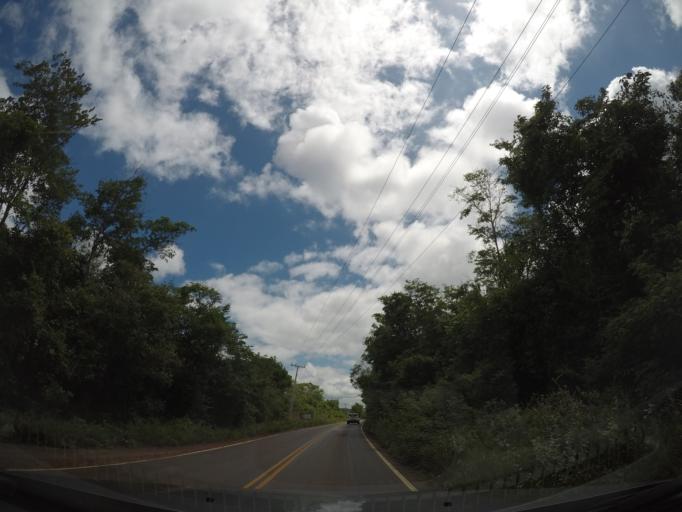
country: BR
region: Bahia
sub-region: Iraquara
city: Iraquara
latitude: -12.4804
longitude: -41.3621
